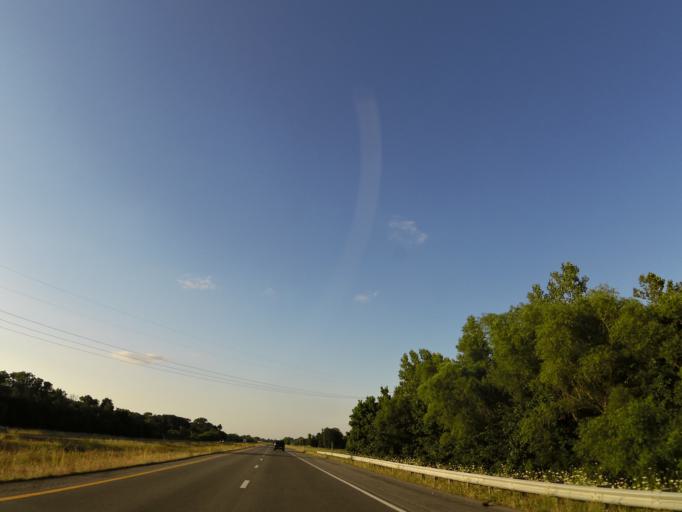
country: US
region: Tennessee
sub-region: Wilson County
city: Lebanon
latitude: 36.1575
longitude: -86.3600
